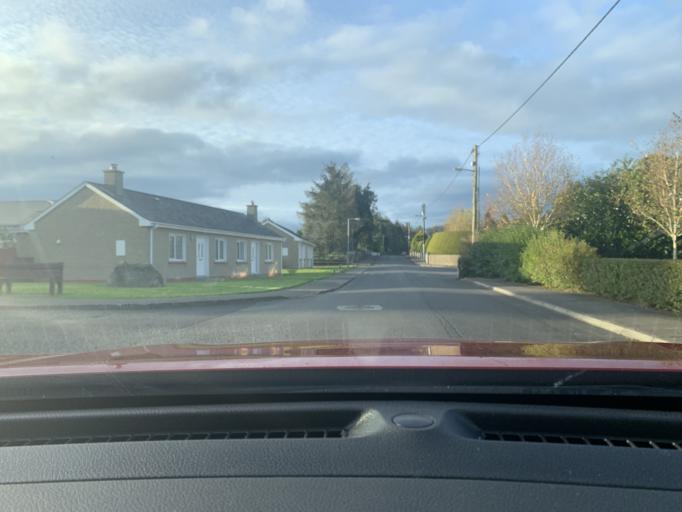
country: IE
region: Connaught
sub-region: Roscommon
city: Ballaghaderreen
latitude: 53.9042
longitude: -8.5759
